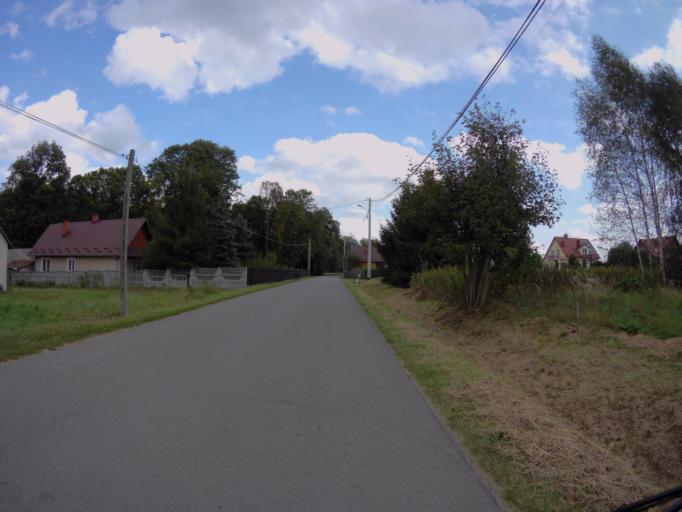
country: PL
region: Subcarpathian Voivodeship
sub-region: Powiat lezajski
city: Brzoza Krolewska
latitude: 50.2442
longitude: 22.3367
